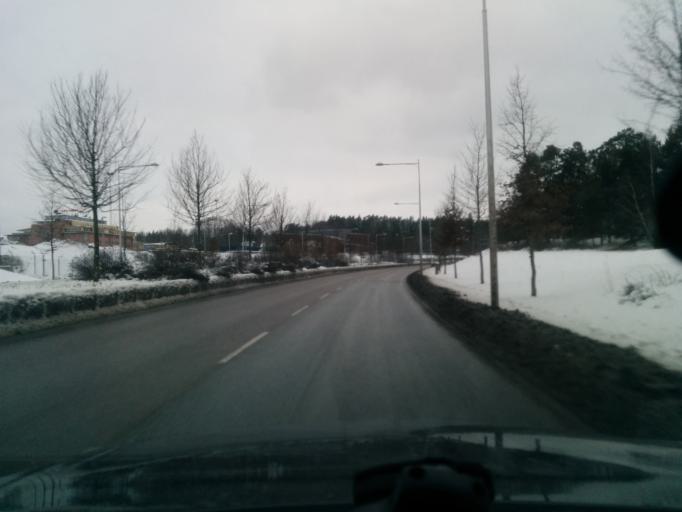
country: SE
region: Stockholm
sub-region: Taby Kommun
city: Taby
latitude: 59.4502
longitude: 18.0887
